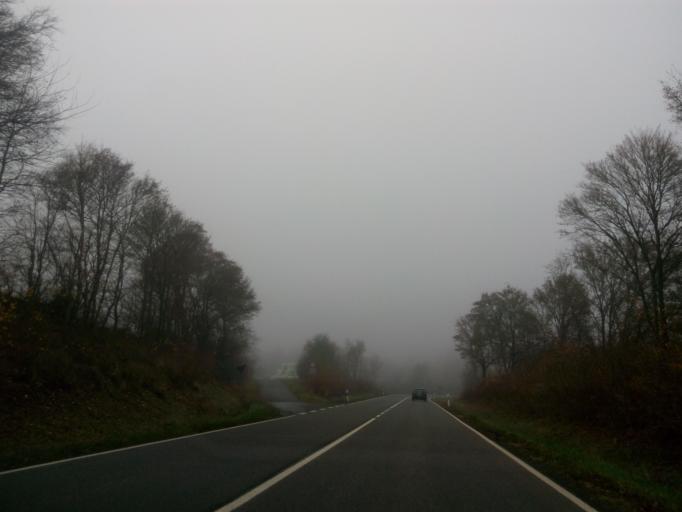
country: DE
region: Rheinland-Pfalz
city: Sien
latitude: 49.6908
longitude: 7.5123
